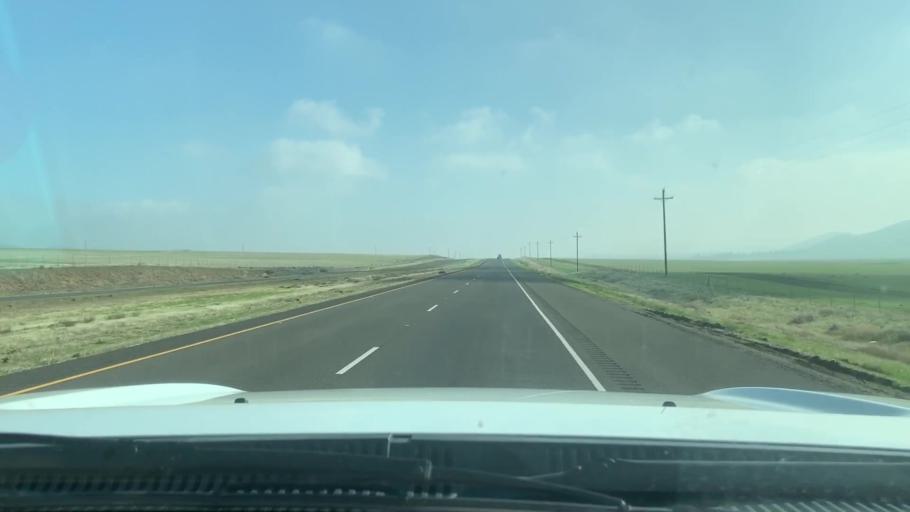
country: US
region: California
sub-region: San Luis Obispo County
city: Shandon
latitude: 35.6992
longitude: -120.1413
